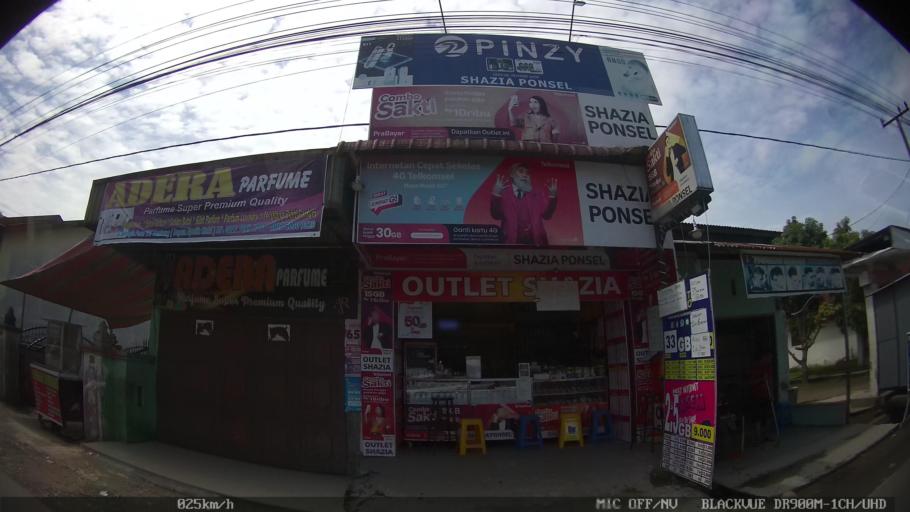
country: ID
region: North Sumatra
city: Medan
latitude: 3.5910
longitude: 98.7433
